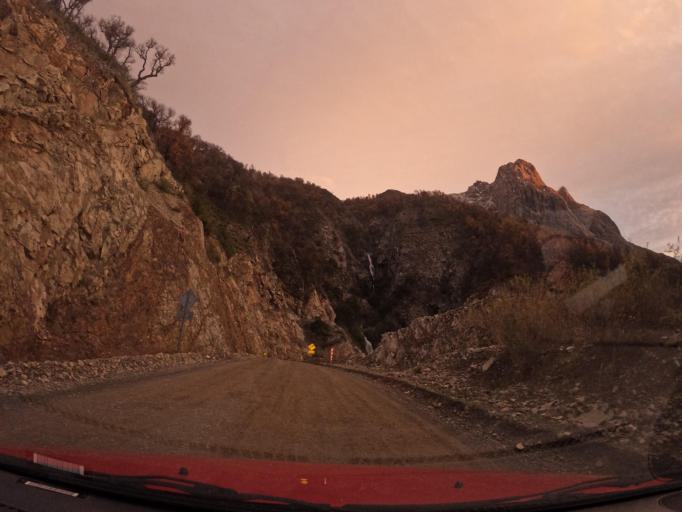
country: CL
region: Maule
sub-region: Provincia de Linares
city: Colbun
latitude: -35.8565
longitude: -71.1689
